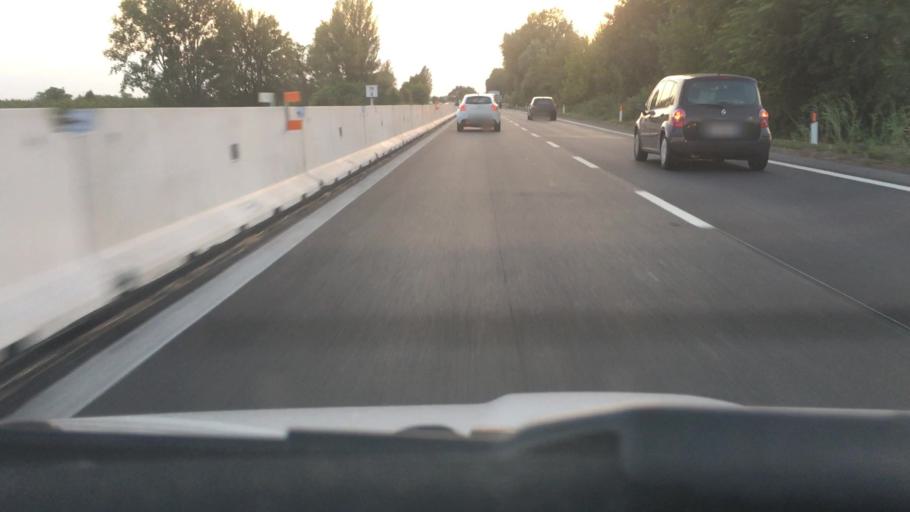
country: IT
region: Emilia-Romagna
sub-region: Provincia di Ferrara
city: Gaibanella-Sant'Edigio
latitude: 44.7984
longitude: 11.6597
